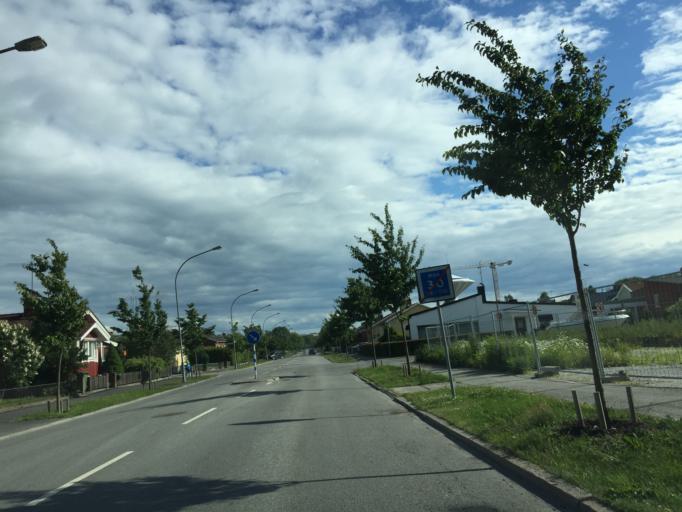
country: SE
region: OErebro
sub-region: Orebro Kommun
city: Orebro
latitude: 59.2930
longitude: 15.2280
